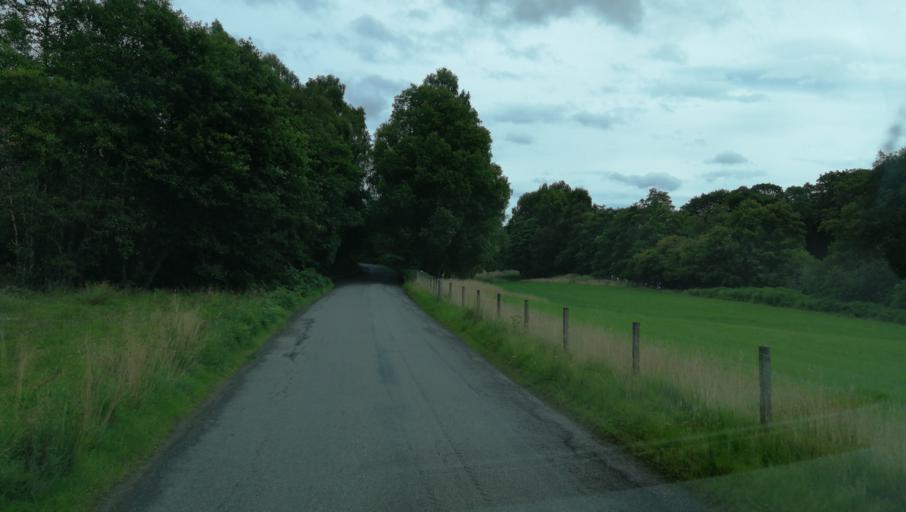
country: GB
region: Scotland
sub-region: Highland
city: Beauly
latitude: 57.3337
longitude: -4.7868
